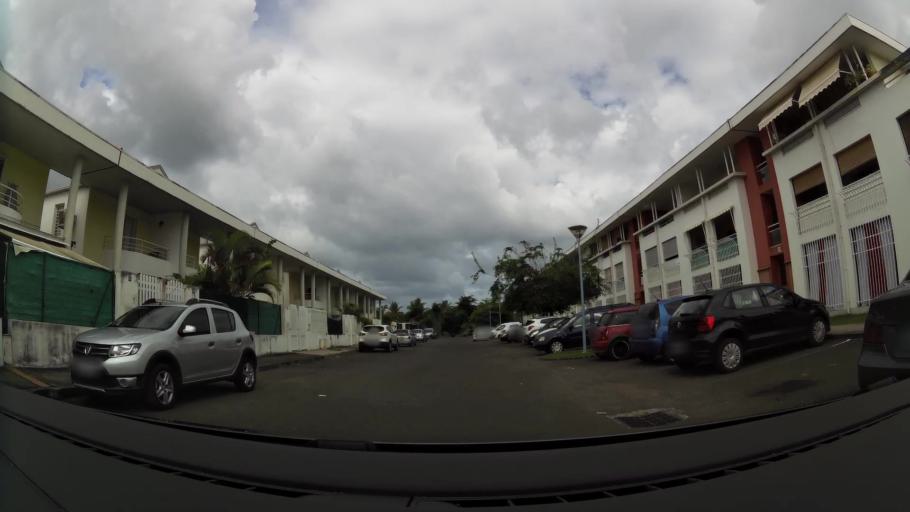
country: GP
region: Guadeloupe
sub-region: Guadeloupe
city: Baie-Mahault
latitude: 16.2555
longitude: -61.5863
